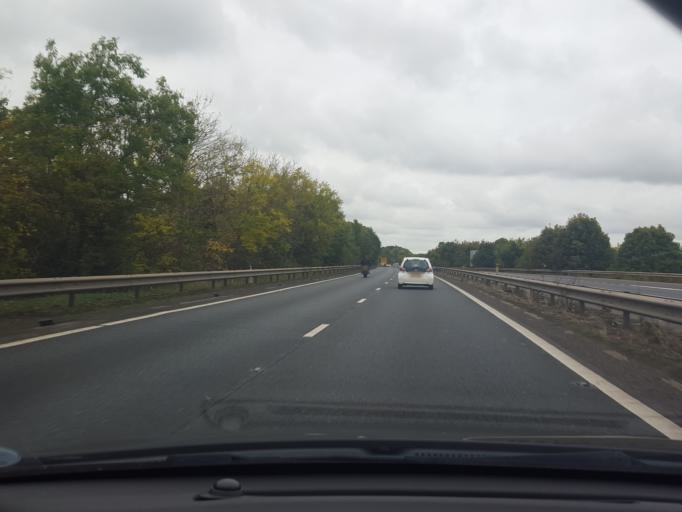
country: GB
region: England
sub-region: Suffolk
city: Needham Market
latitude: 52.1489
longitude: 1.0762
